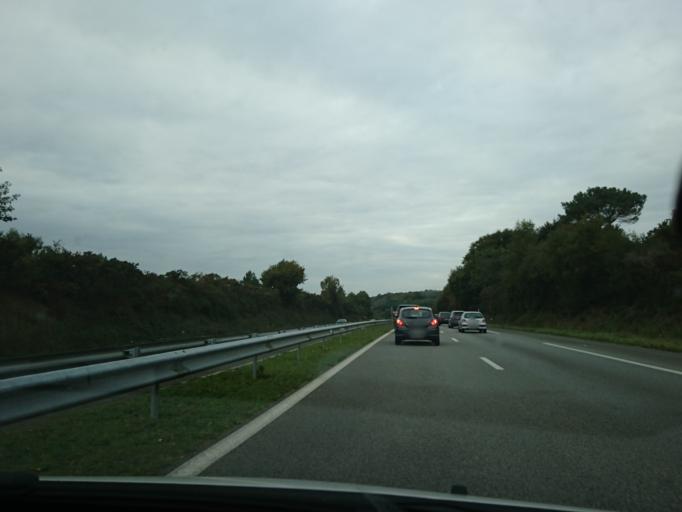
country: FR
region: Brittany
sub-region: Departement du Morbihan
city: Muzillac
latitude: 47.5456
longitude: -2.4377
